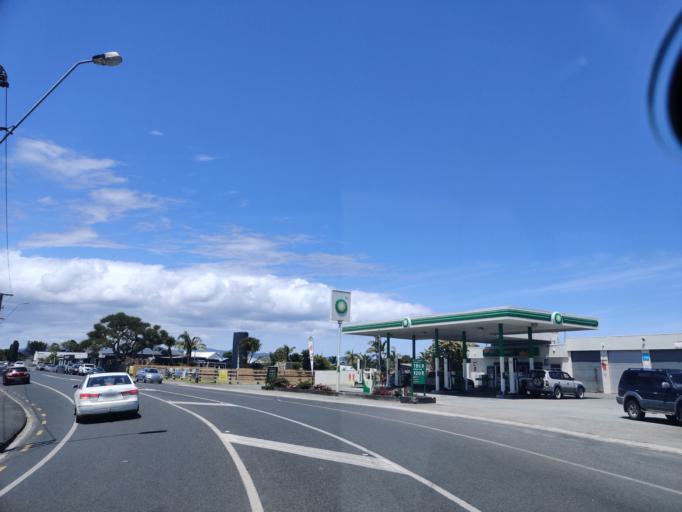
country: NZ
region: Northland
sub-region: Far North District
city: Kaitaia
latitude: -35.0473
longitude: 173.2562
